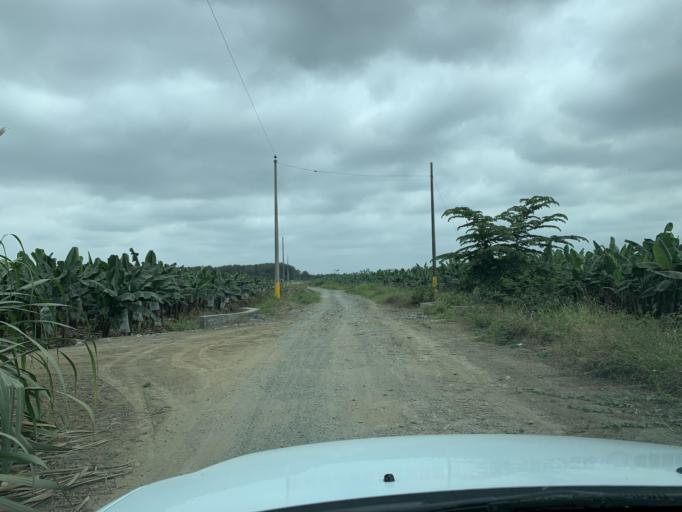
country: EC
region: Guayas
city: Coronel Marcelino Mariduena
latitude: -2.3333
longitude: -79.4550
